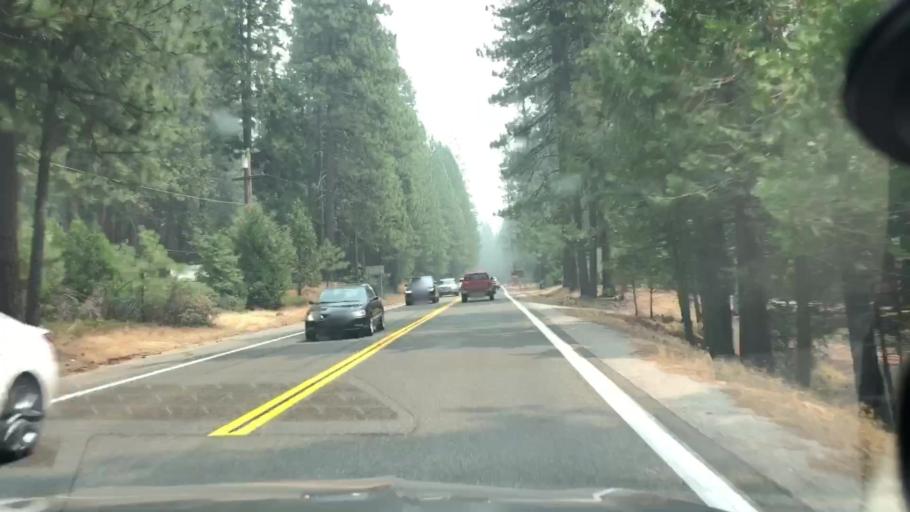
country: US
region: California
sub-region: El Dorado County
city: Pollock Pines
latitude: 38.7705
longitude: -120.3108
